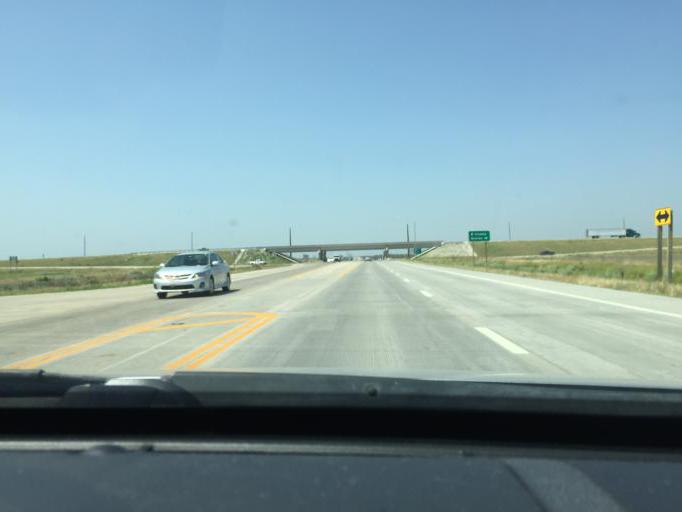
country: US
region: Kansas
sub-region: Reno County
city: Hutchinson
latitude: 38.0260
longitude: -97.8669
